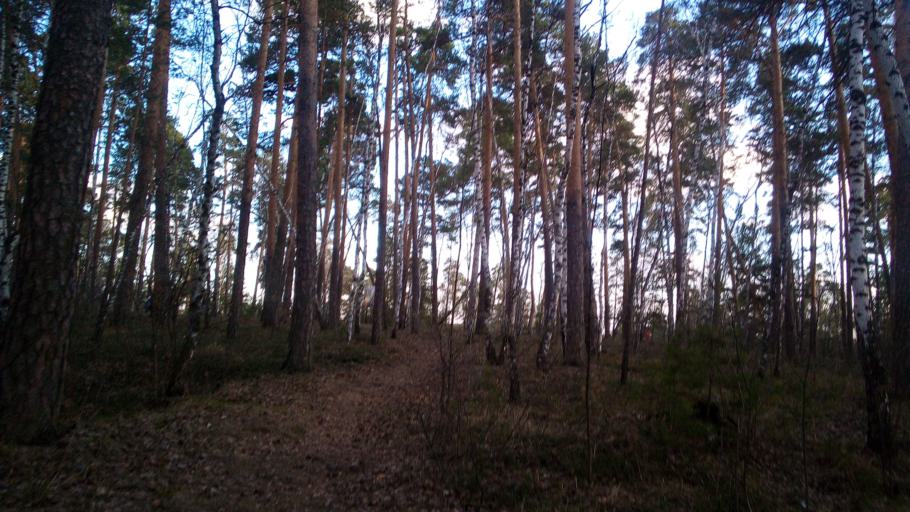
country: RU
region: Chelyabinsk
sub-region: Gorod Chelyabinsk
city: Chelyabinsk
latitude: 55.1606
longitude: 61.3231
